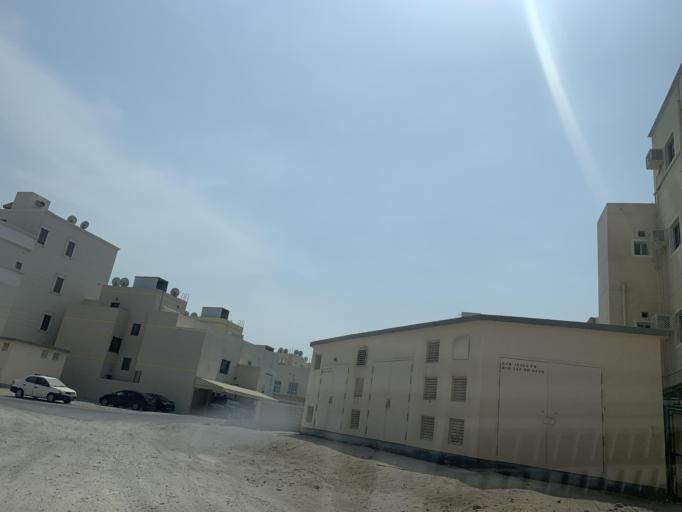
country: BH
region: Muharraq
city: Al Hadd
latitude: 26.2671
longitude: 50.6568
